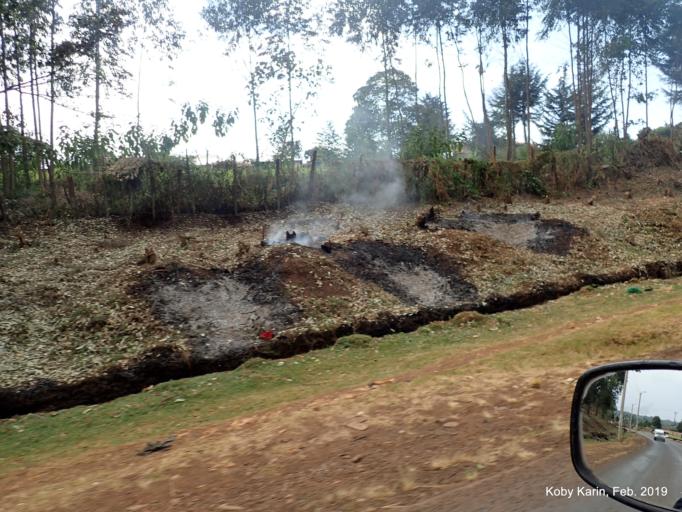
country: KE
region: Kericho
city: Litein
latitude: -0.6466
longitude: 35.1926
